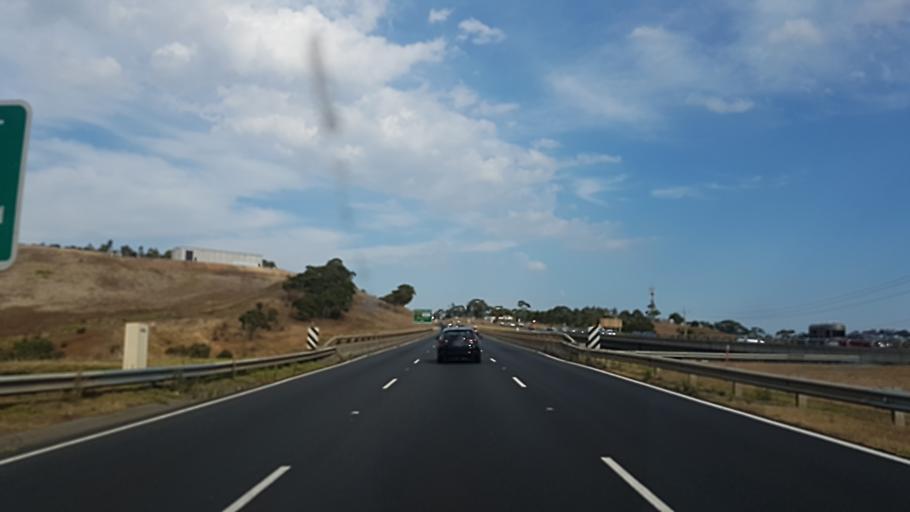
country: AU
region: Victoria
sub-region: Brimbank
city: Keilor
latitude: -37.7194
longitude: 144.8397
